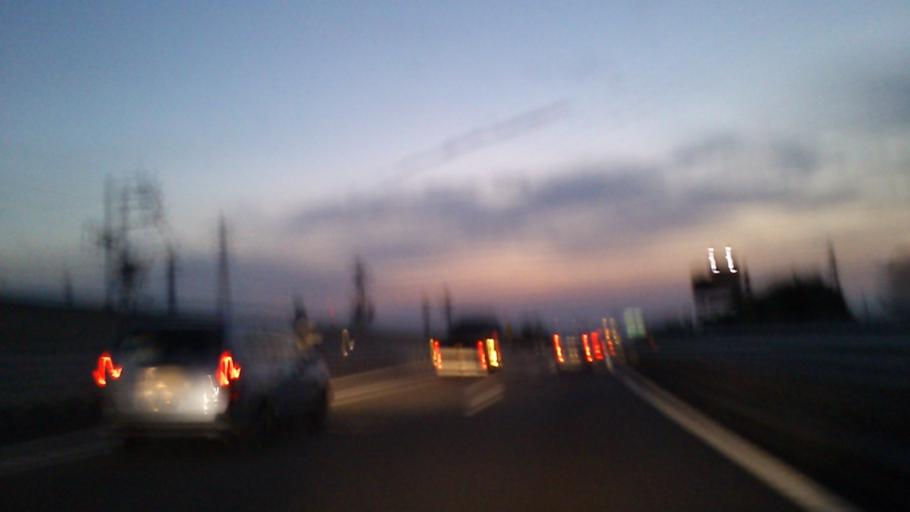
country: JP
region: Aichi
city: Komaki
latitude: 35.2982
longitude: 136.9248
